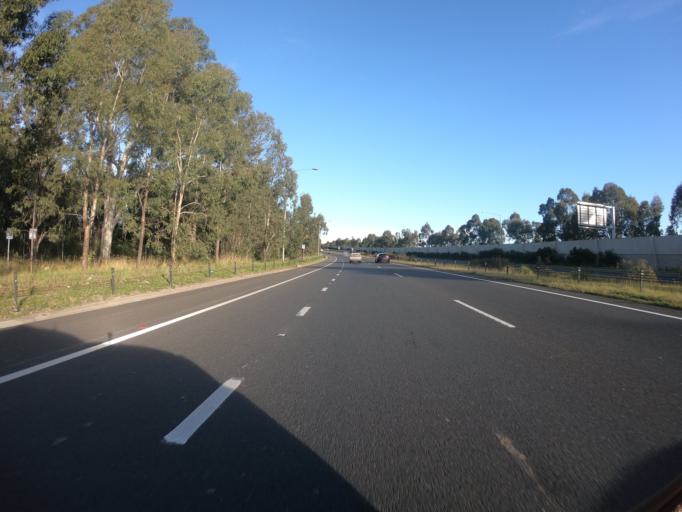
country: AU
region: New South Wales
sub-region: Blacktown
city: Glendenning
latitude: -33.7659
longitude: 150.8462
